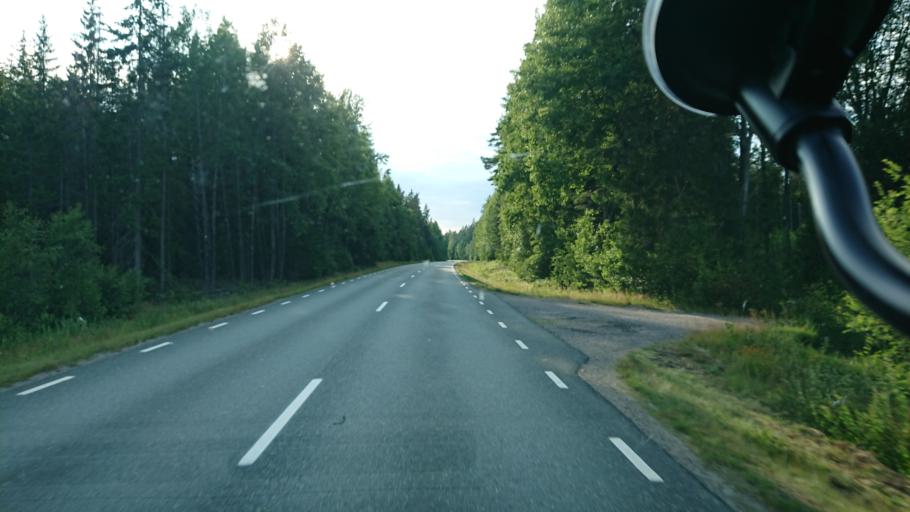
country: SE
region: Kronoberg
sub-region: Vaxjo Kommun
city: Rottne
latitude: 57.0354
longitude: 14.9257
